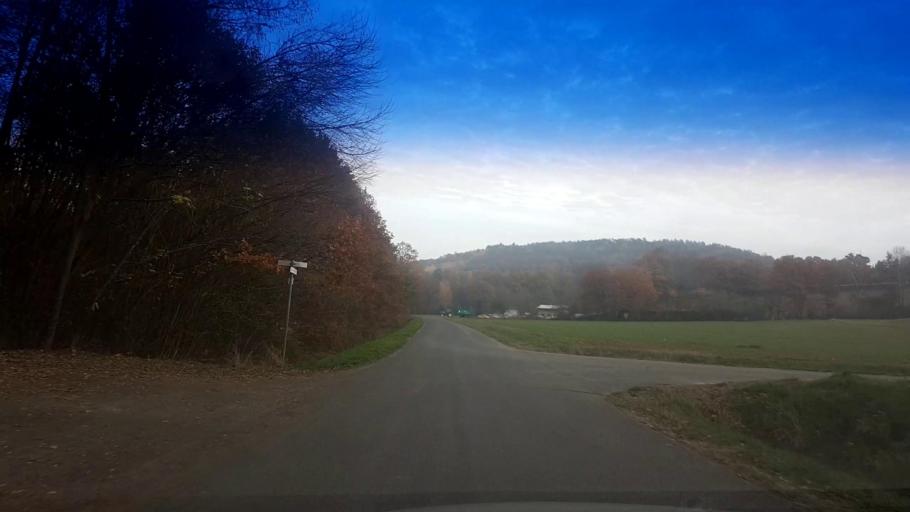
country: DE
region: Bavaria
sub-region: Upper Franconia
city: Viereth-Trunstadt
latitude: 49.9203
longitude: 10.7609
